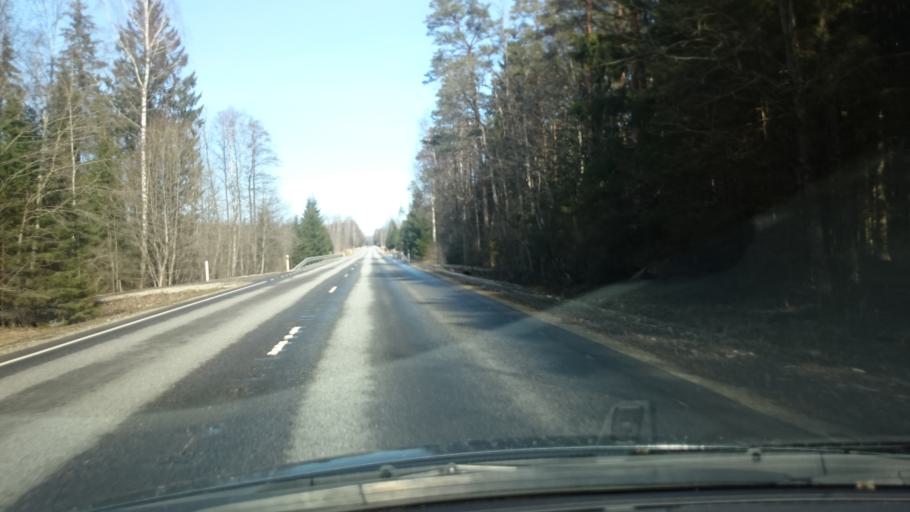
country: EE
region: Jaervamaa
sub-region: Tueri vald
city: Sarevere
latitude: 58.7030
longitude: 25.2622
